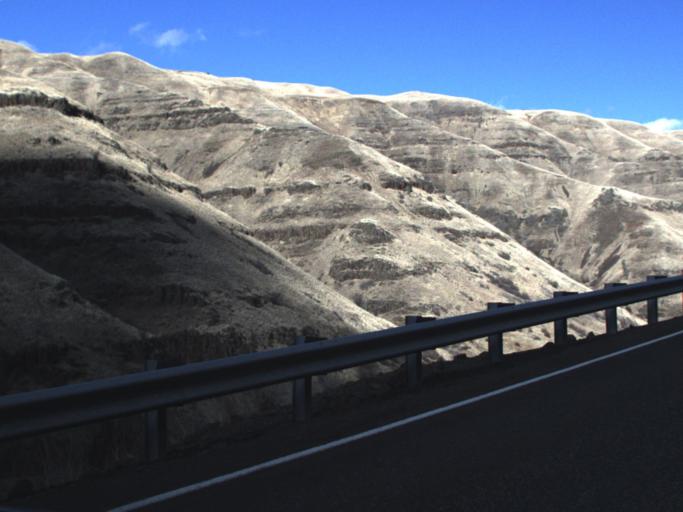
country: US
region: Washington
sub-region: Asotin County
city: Asotin
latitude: 46.0013
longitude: -117.2789
